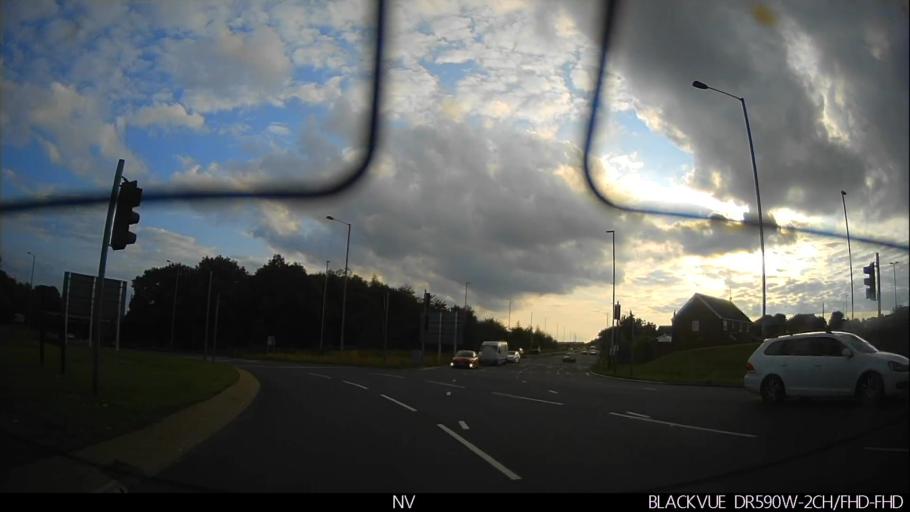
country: GB
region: England
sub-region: City and Borough of Leeds
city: Gildersome
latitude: 53.7496
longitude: -1.6352
